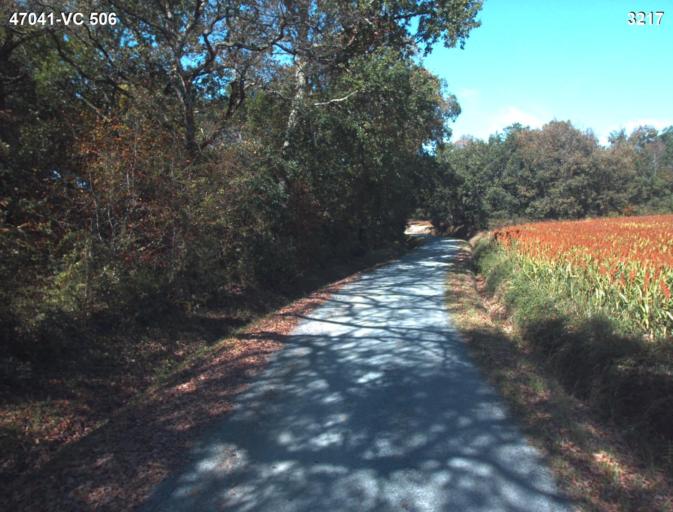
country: FR
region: Aquitaine
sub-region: Departement du Lot-et-Garonne
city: Vianne
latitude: 44.1900
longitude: 0.3822
